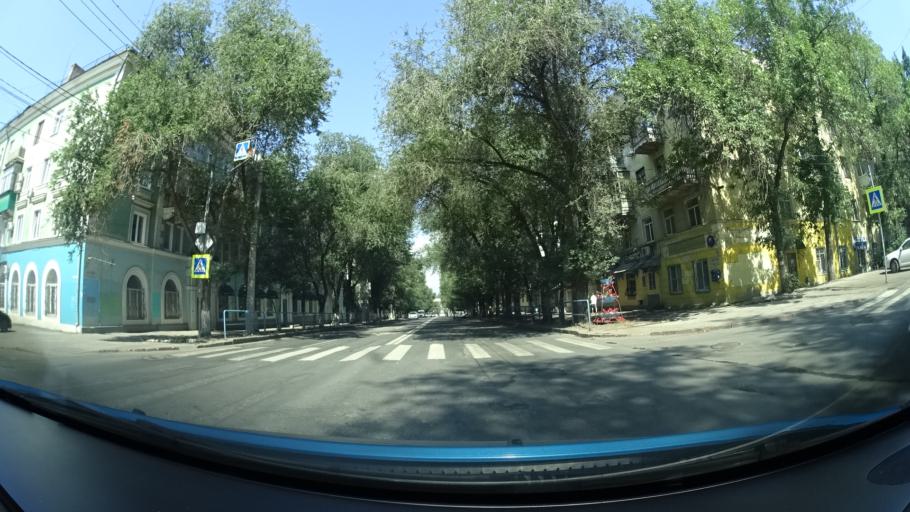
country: RU
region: Samara
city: Samara
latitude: 53.2086
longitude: 50.1588
